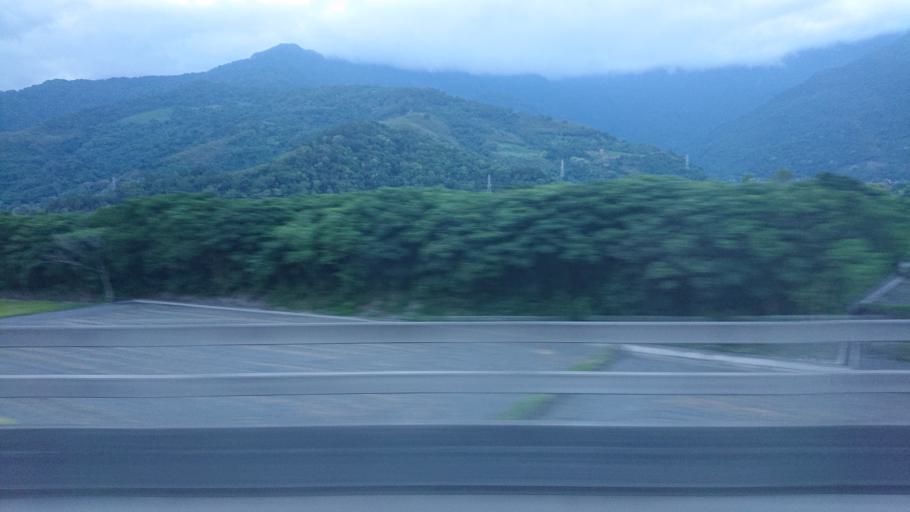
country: TW
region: Taiwan
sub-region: Taitung
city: Taitung
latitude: 23.0294
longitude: 121.1593
